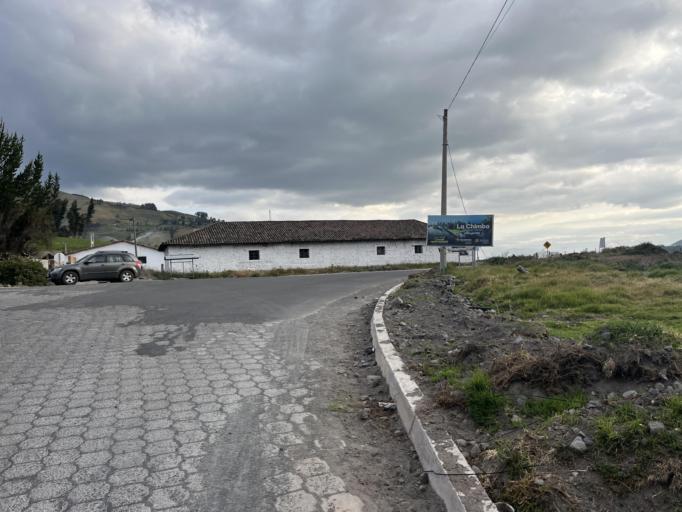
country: EC
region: Pichincha
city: Cayambe
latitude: 0.1383
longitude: -78.0677
